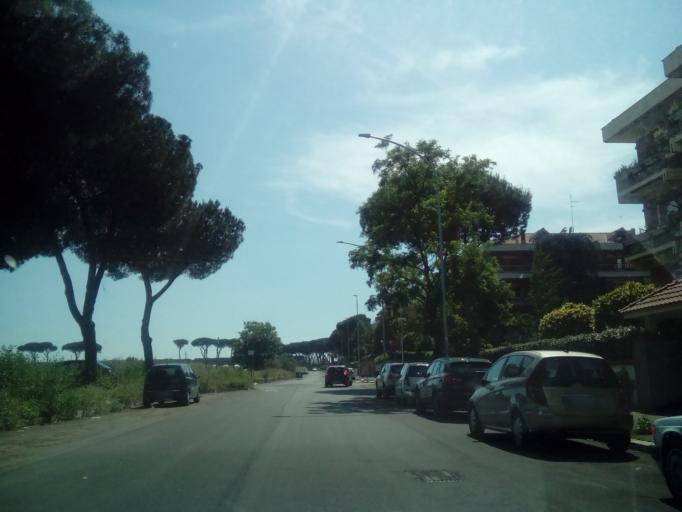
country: IT
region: Latium
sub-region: Citta metropolitana di Roma Capitale
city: Ciampino
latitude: 41.8497
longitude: 12.5661
